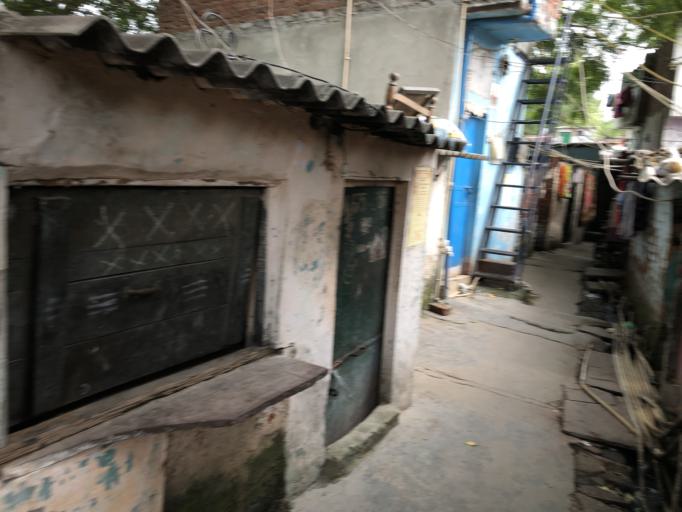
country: IN
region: NCT
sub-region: New Delhi
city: New Delhi
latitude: 28.5780
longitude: 77.2500
